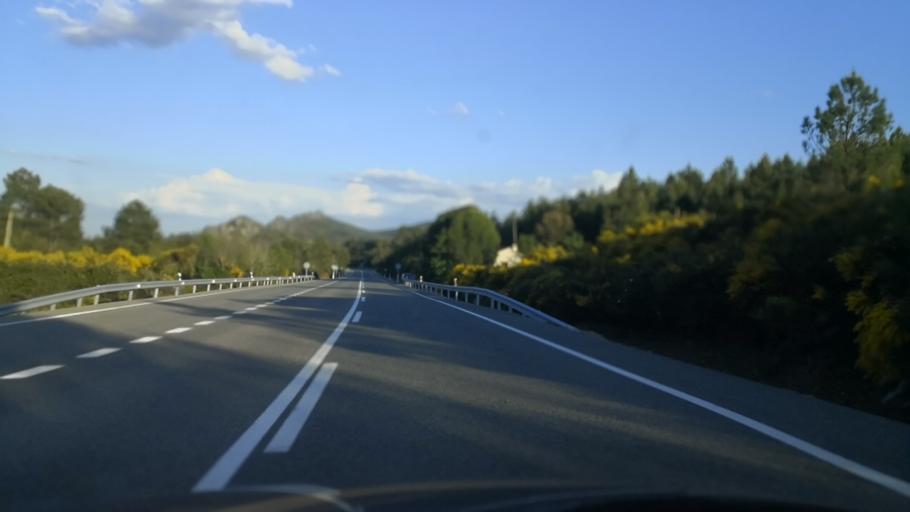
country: PT
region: Portalegre
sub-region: Portalegre
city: Sao Juliao
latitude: 39.3457
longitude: -7.2981
